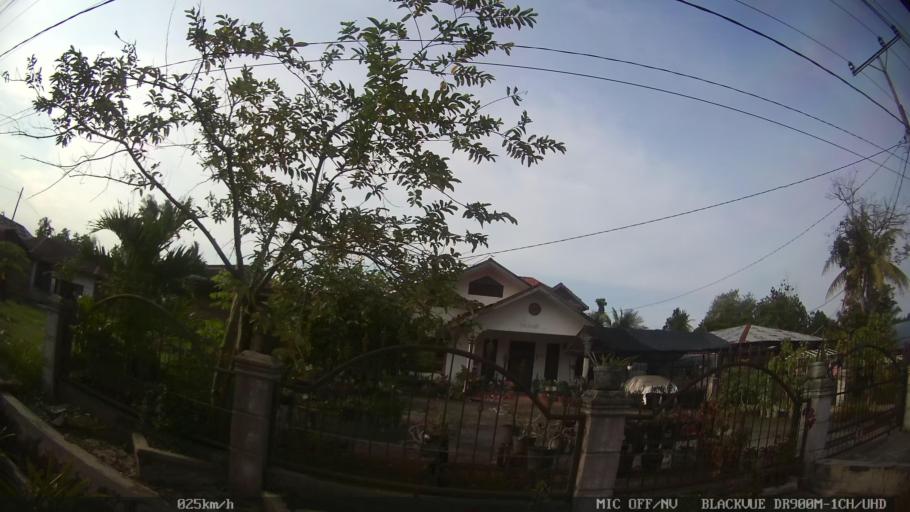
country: ID
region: North Sumatra
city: Binjai
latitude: 3.6175
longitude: 98.5316
